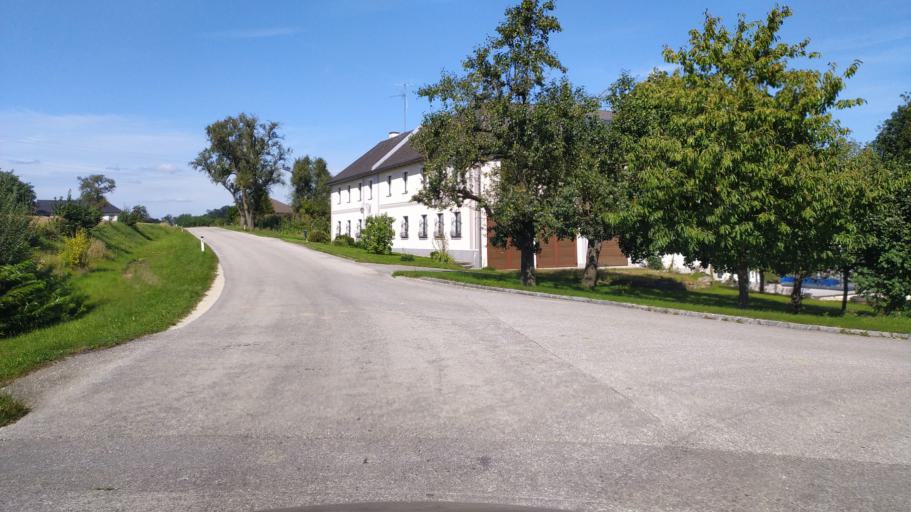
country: AT
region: Lower Austria
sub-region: Politischer Bezirk Amstetten
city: Strengberg
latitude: 48.1300
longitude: 14.6726
